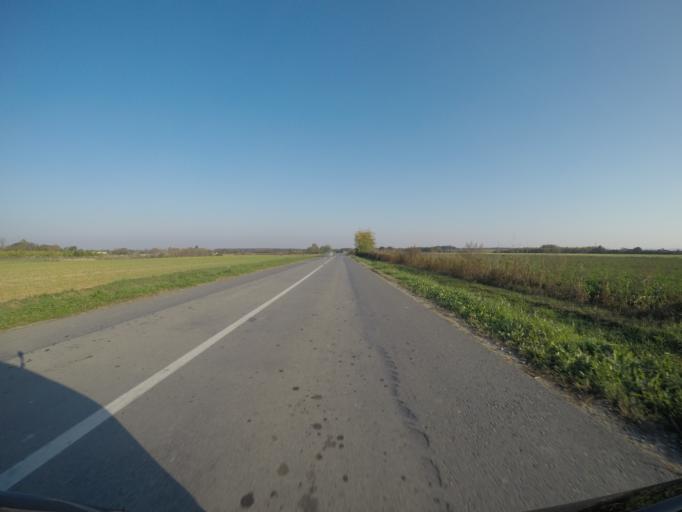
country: HR
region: Virovitick-Podravska
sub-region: Grad Virovitica
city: Virovitica
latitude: 45.8849
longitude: 17.3828
